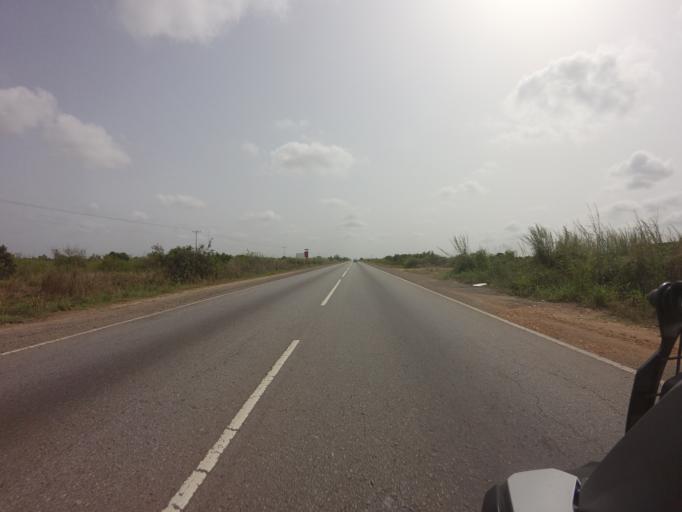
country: GH
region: Greater Accra
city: Tema
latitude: 5.7892
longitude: 0.1125
